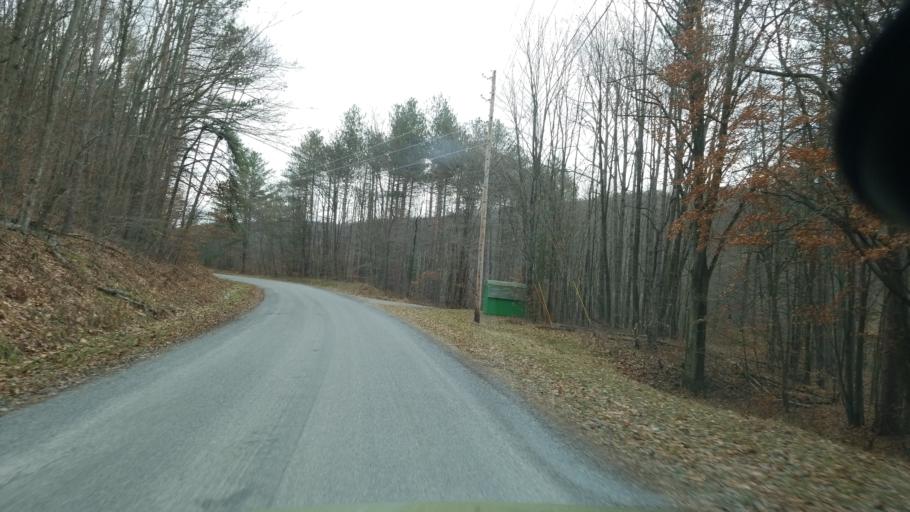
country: US
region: Pennsylvania
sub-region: Clearfield County
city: Treasure Lake
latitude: 41.1128
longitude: -78.6277
